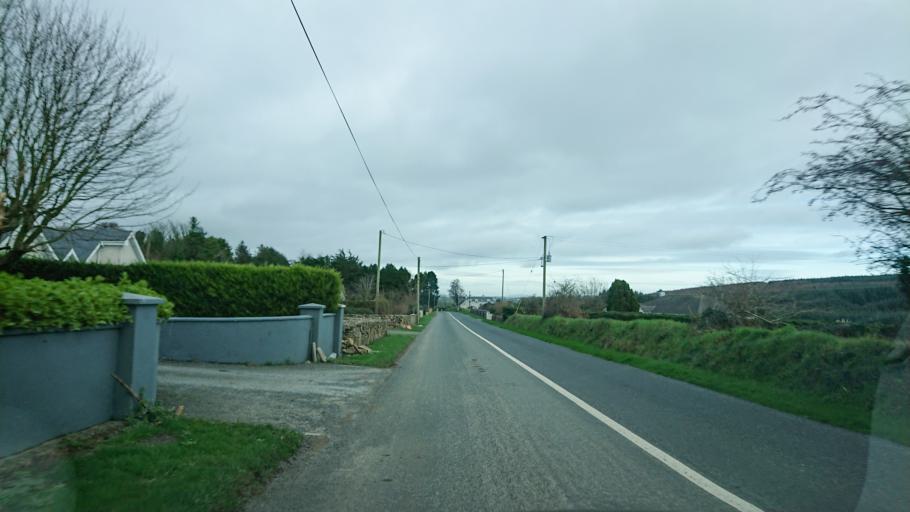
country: IE
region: Leinster
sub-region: Kilkenny
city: Mooncoin
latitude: 52.2056
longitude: -7.2512
